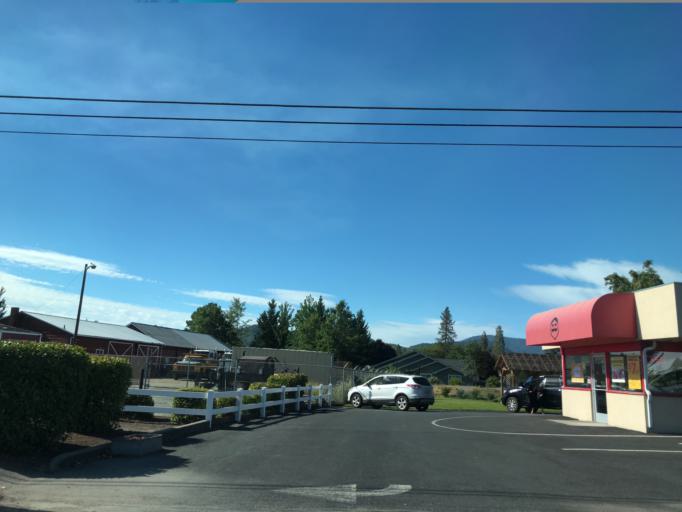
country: US
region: Oregon
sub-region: Josephine County
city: Grants Pass
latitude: 42.4240
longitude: -123.3380
